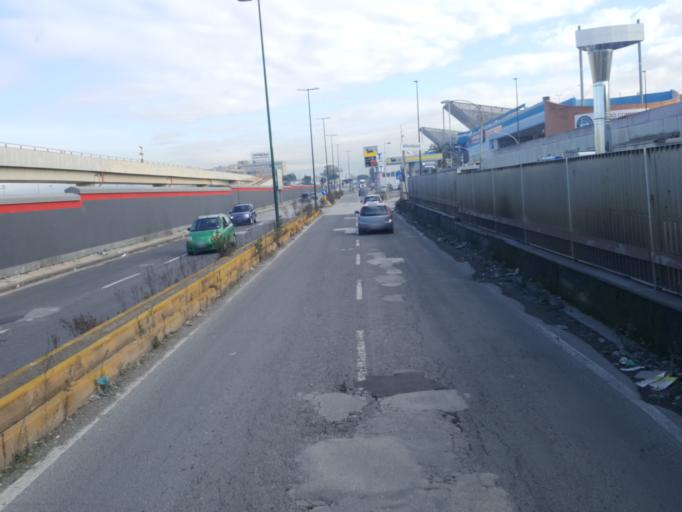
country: IT
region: Campania
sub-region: Provincia di Napoli
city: San Giorgio a Cremano
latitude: 40.8494
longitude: 14.3080
